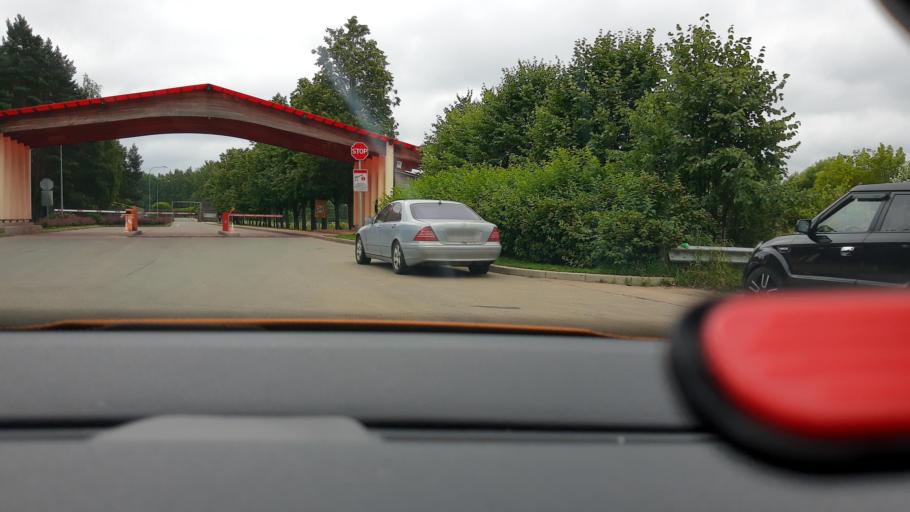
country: RU
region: Moskovskaya
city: Pirogovskiy
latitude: 55.9926
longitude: 37.6732
